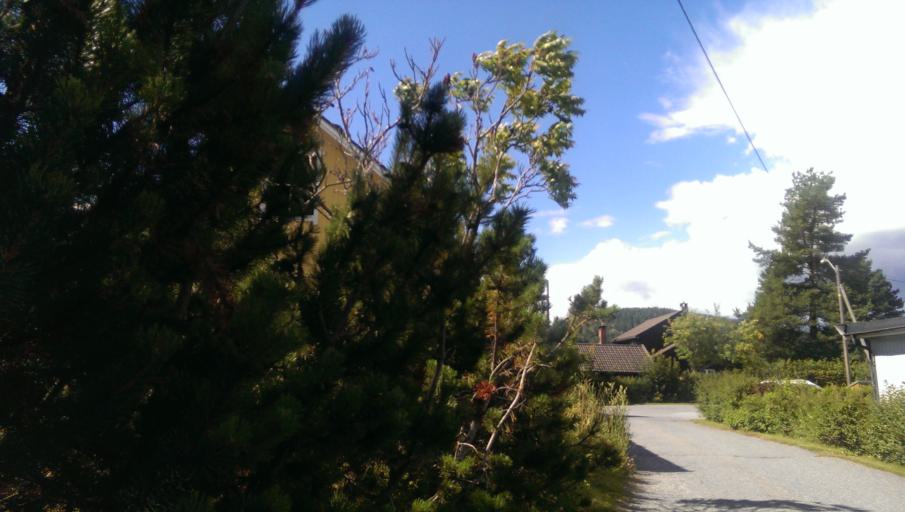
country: NO
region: Buskerud
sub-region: Kongsberg
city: Kongsberg
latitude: 59.6565
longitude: 9.6555
